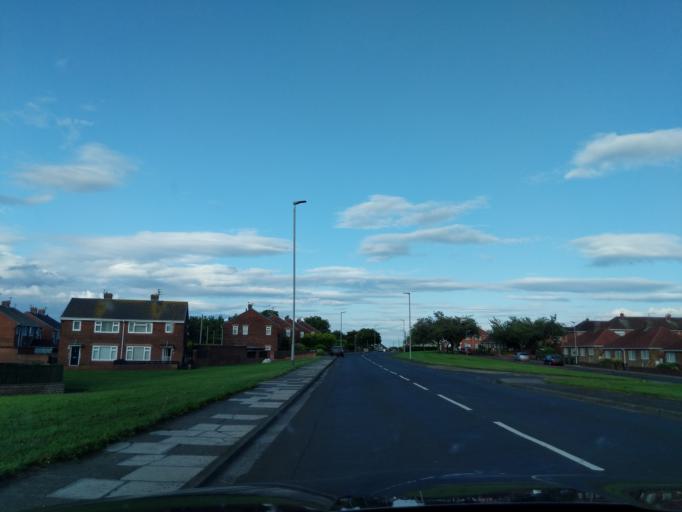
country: GB
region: England
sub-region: Northumberland
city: Bedlington
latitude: 55.1328
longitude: -1.5777
